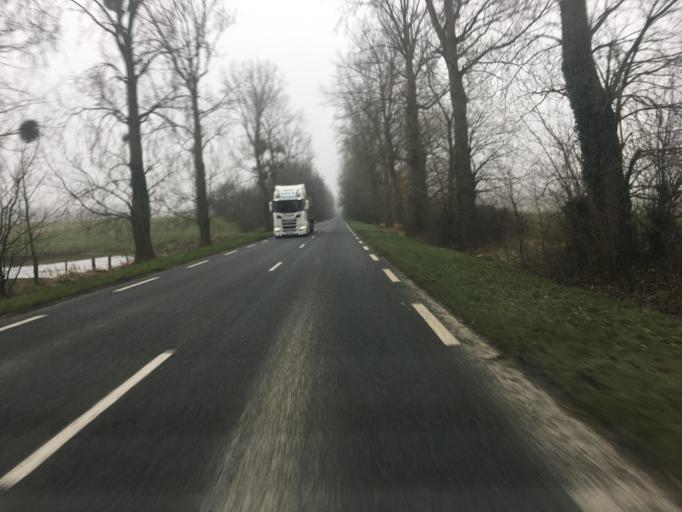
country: FR
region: Haute-Normandie
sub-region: Departement de la Seine-Maritime
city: La Remuee
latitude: 49.5232
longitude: 0.4201
